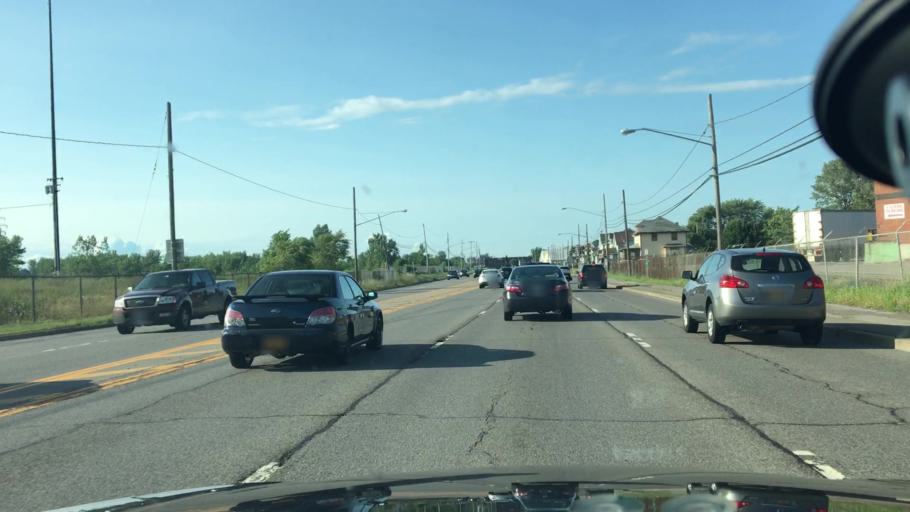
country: US
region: New York
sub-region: Erie County
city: Blasdell
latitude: 42.8088
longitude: -78.8459
